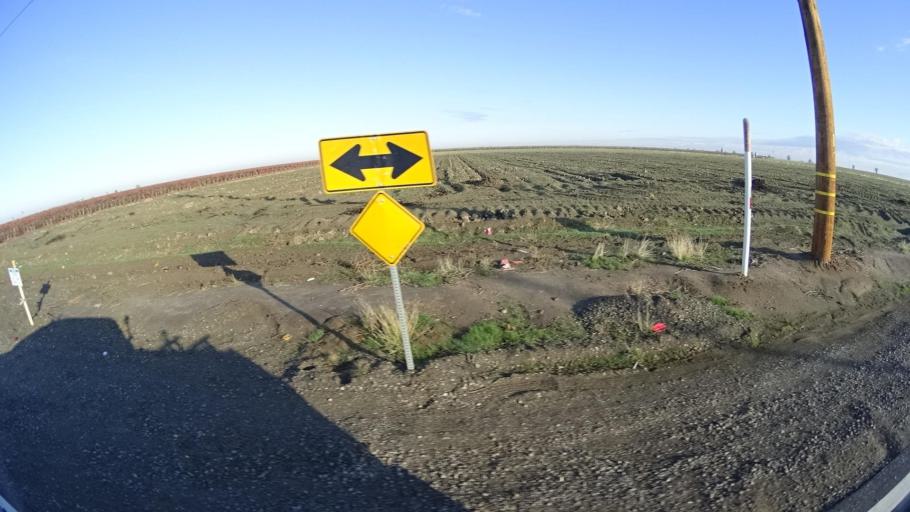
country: US
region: California
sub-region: Kern County
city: Delano
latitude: 35.7904
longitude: -119.2763
